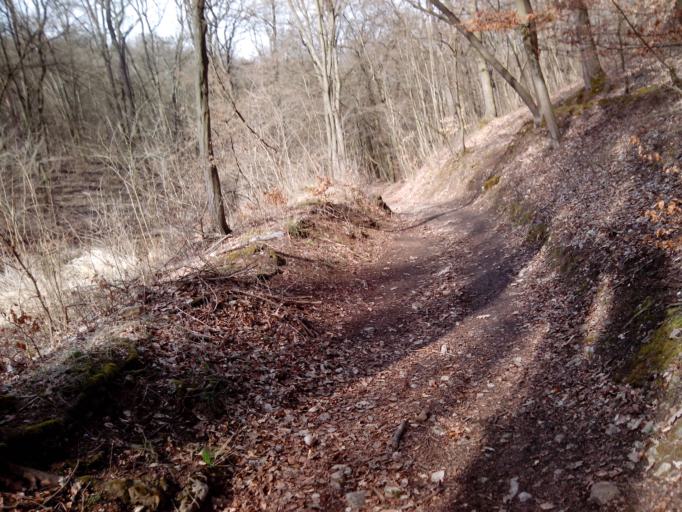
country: CZ
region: Central Bohemia
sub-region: Okres Beroun
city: Beroun
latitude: 49.9410
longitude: 14.1042
